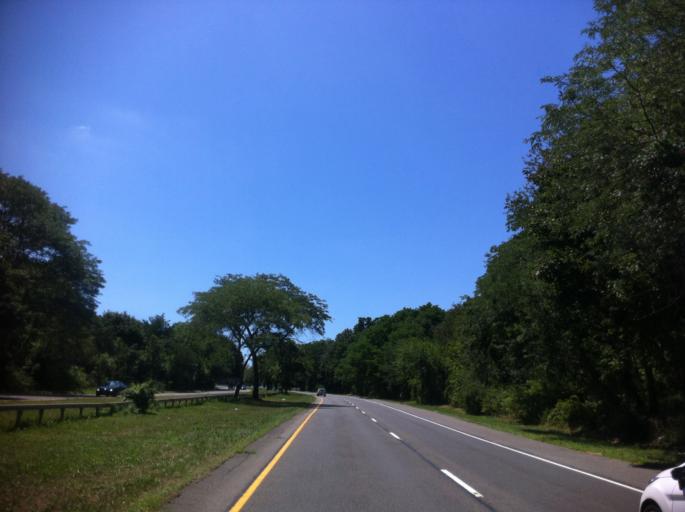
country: US
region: New York
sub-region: Nassau County
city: Glen Head
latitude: 40.8303
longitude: -73.6217
